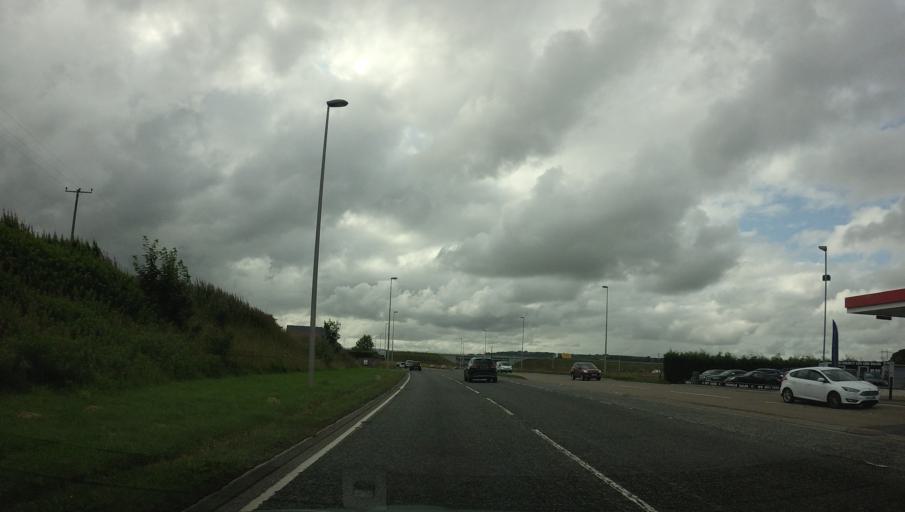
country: GB
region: Scotland
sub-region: Aberdeenshire
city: Westhill
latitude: 57.1468
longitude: -2.2380
